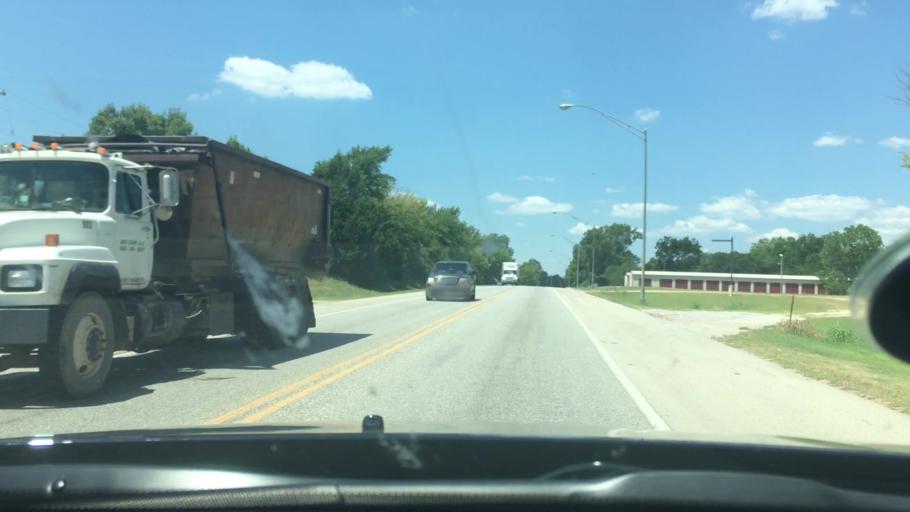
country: US
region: Oklahoma
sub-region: Carter County
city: Dickson
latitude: 34.1863
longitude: -96.8868
